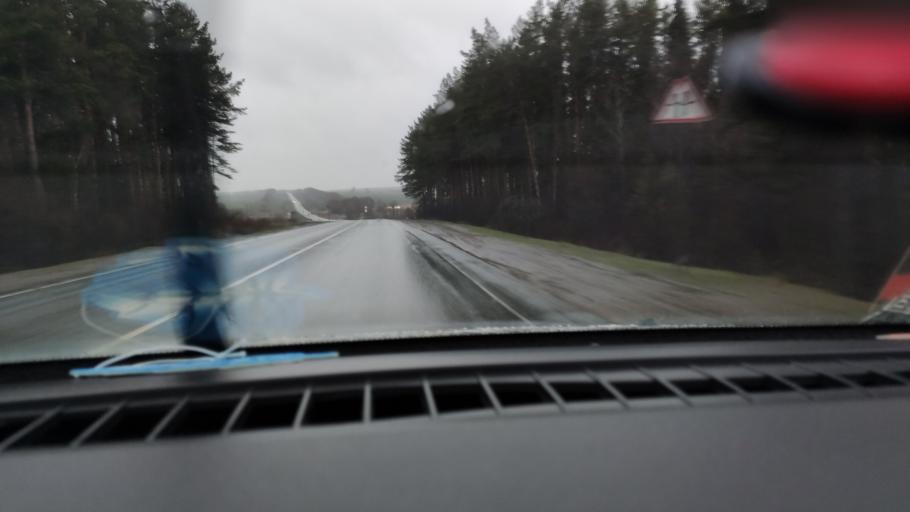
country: RU
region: Tatarstan
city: Mendeleyevsk
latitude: 55.9407
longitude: 52.2909
